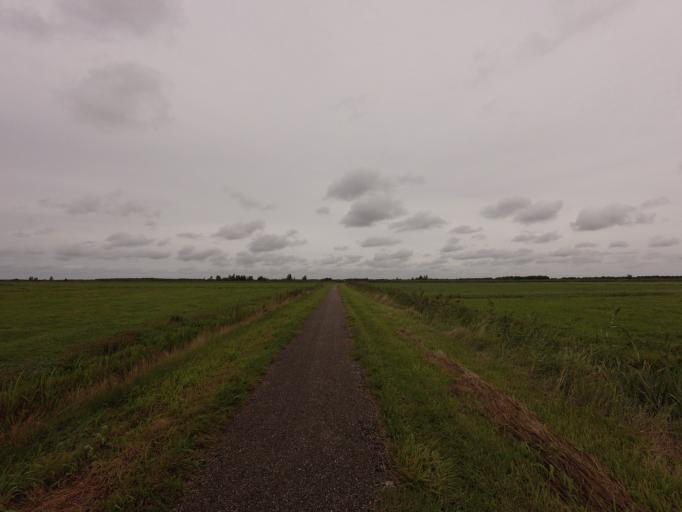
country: NL
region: Overijssel
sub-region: Gemeente Steenwijkerland
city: Blokzijl
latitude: 52.7625
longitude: 5.9268
